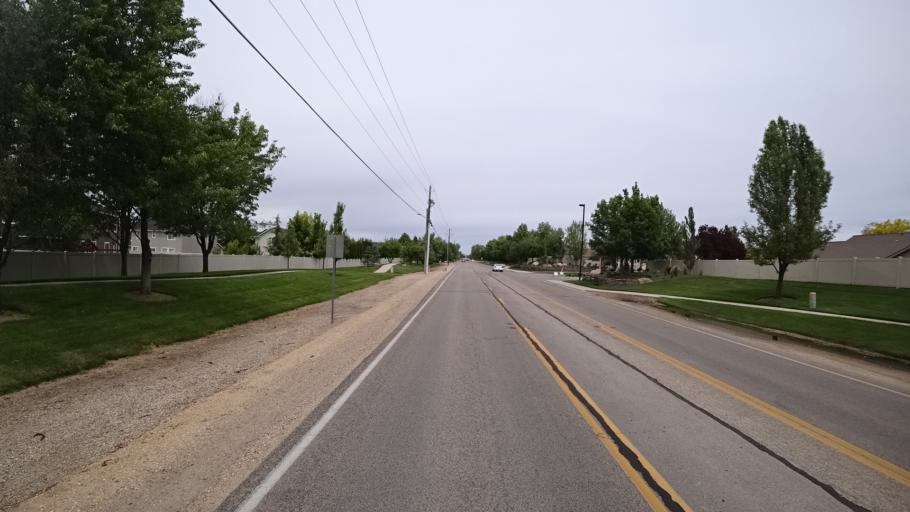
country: US
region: Idaho
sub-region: Ada County
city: Meridian
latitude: 43.5699
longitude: -116.3746
